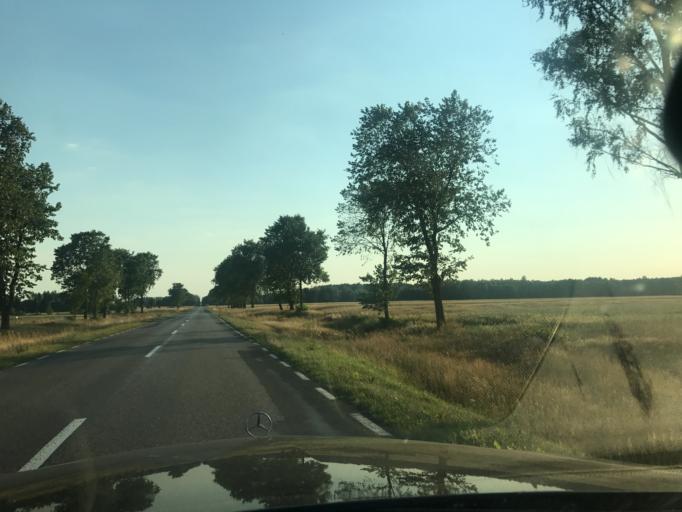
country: PL
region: Lublin Voivodeship
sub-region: Powiat parczewski
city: Jablon
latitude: 51.7327
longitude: 23.1249
